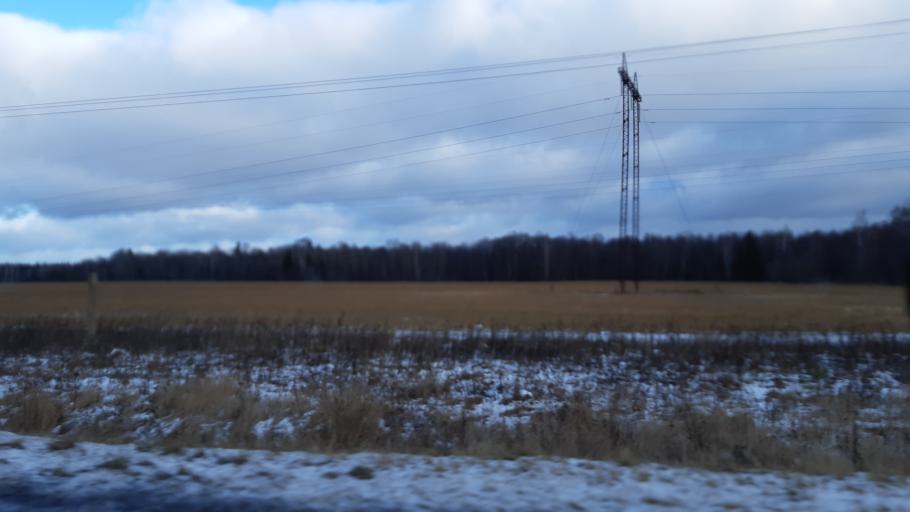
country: RU
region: Moskovskaya
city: Noginsk-9
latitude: 56.0348
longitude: 38.5542
